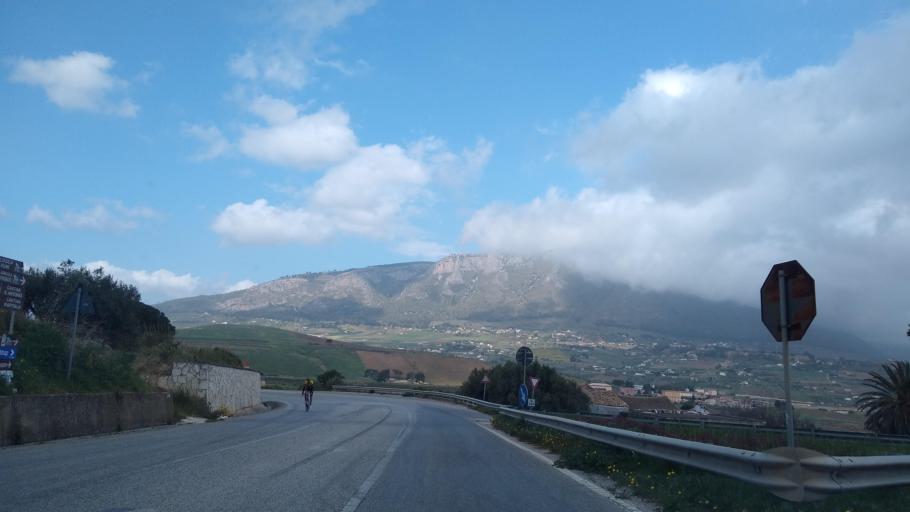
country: IT
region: Sicily
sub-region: Trapani
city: Alcamo
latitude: 37.9726
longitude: 12.9267
